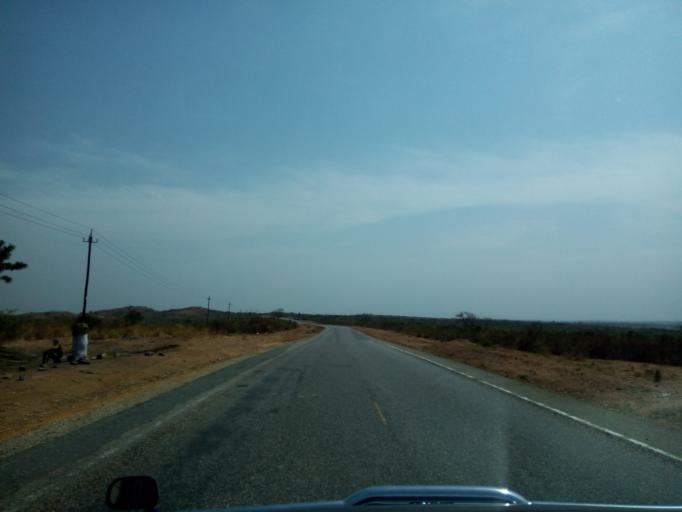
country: UG
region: Northern Region
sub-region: Nebbi District
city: Nebbi
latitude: 2.4466
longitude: 31.2558
